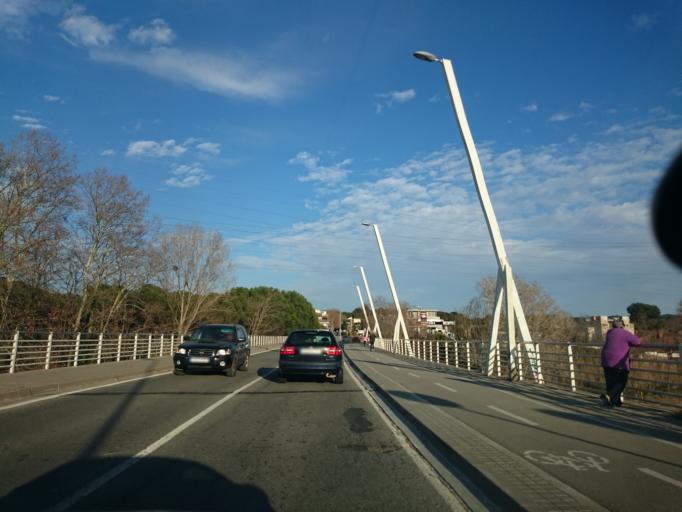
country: ES
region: Catalonia
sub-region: Provincia de Barcelona
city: Cerdanyola del Valles
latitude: 41.4855
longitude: 2.1290
